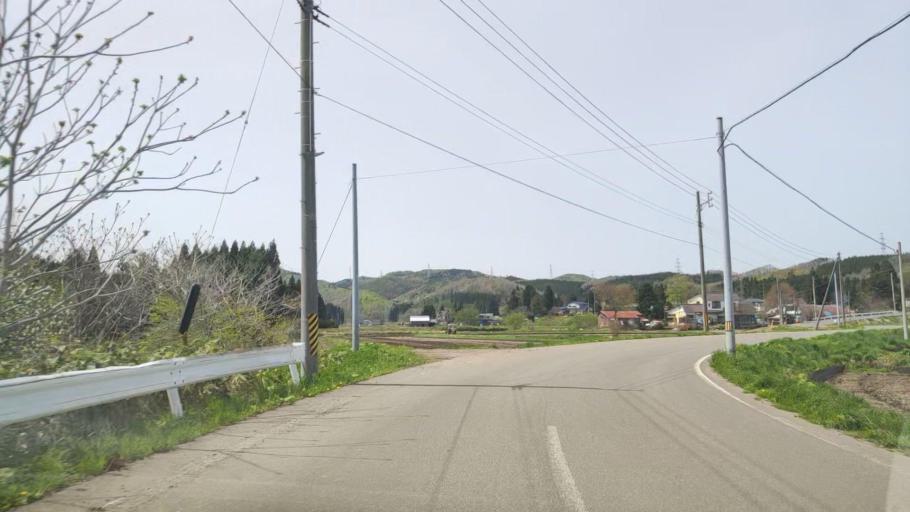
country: JP
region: Aomori
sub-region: Misawa Shi
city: Inuotose
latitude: 40.7869
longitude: 141.1105
